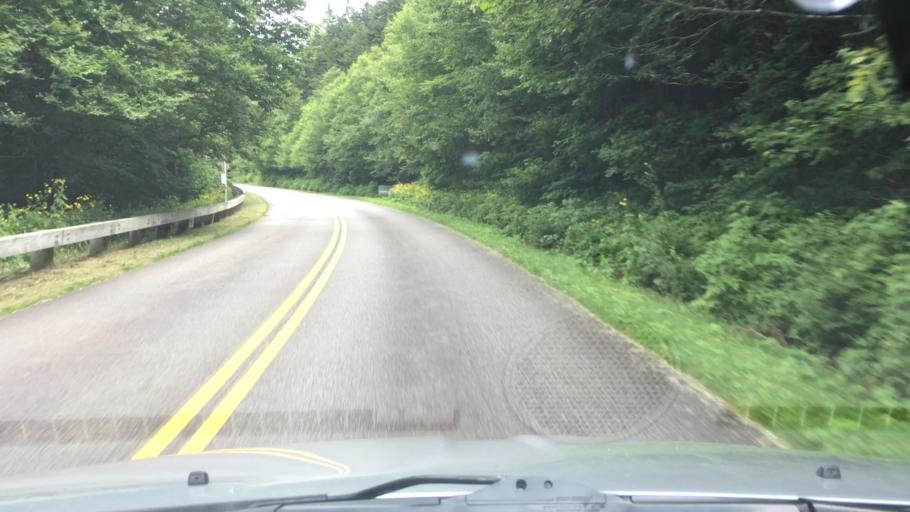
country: US
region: North Carolina
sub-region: Buncombe County
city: Black Mountain
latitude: 35.7166
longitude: -82.2780
